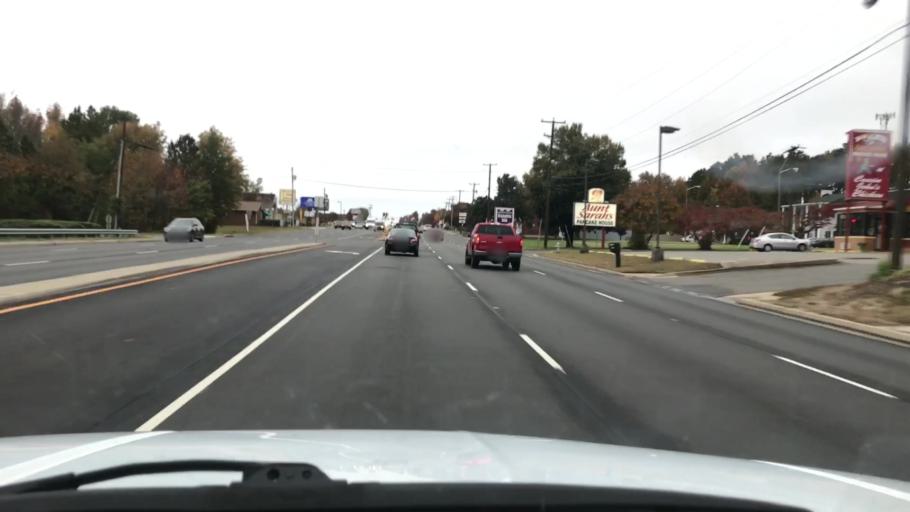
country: US
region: Virginia
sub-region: Henrico County
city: Chamberlayne
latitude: 37.6471
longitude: -77.4599
